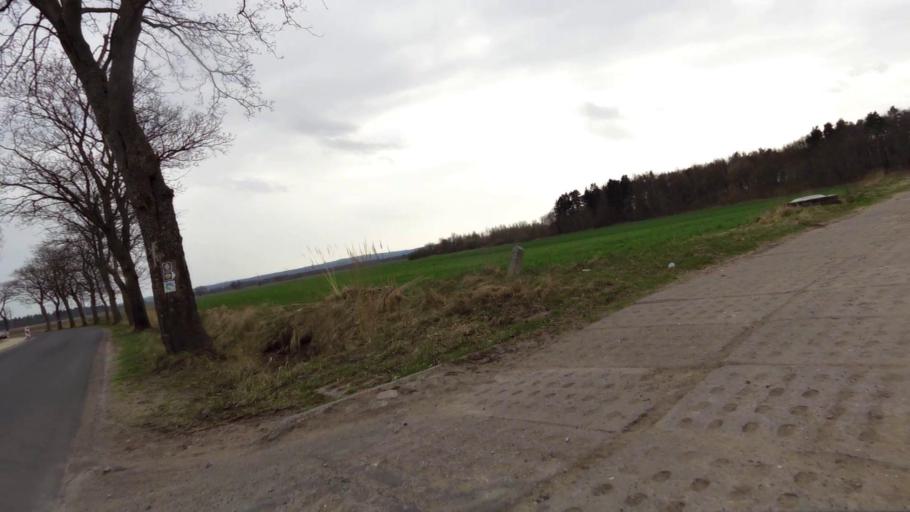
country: PL
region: West Pomeranian Voivodeship
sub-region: Powiat koszalinski
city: Sianow
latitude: 54.2775
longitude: 16.2220
